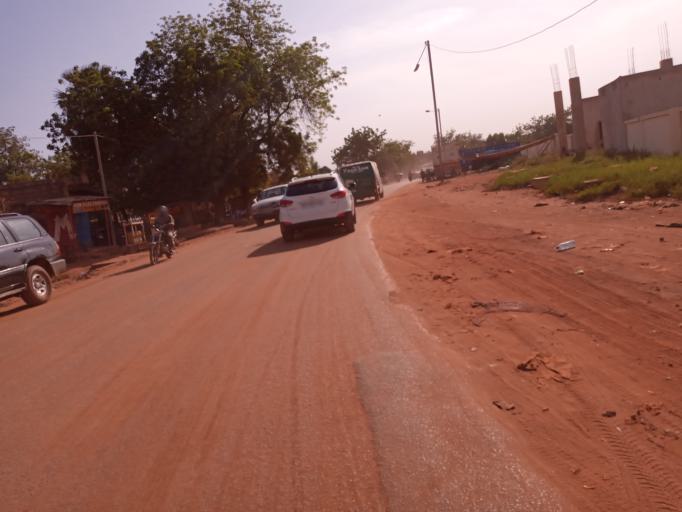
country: ML
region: Bamako
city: Bamako
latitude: 12.6220
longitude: -7.9545
